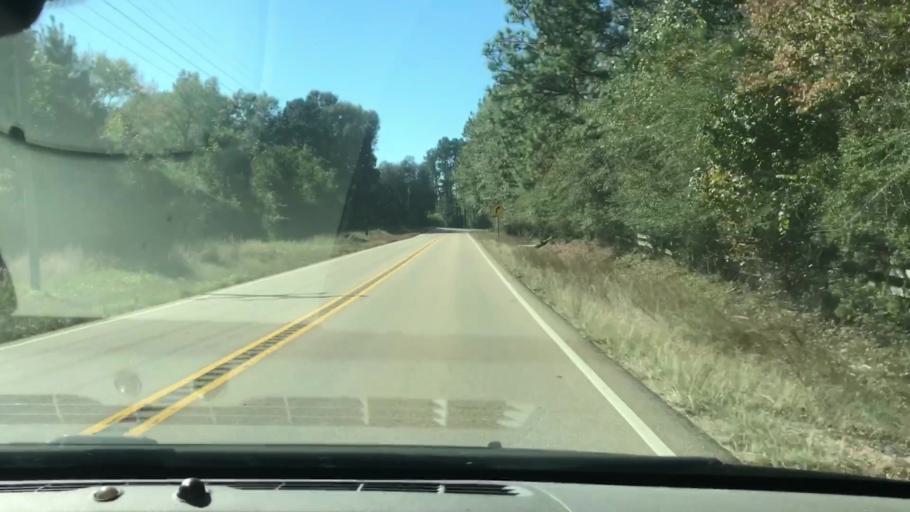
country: US
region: Louisiana
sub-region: Saint Tammany Parish
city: Abita Springs
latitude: 30.5094
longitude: -89.9512
